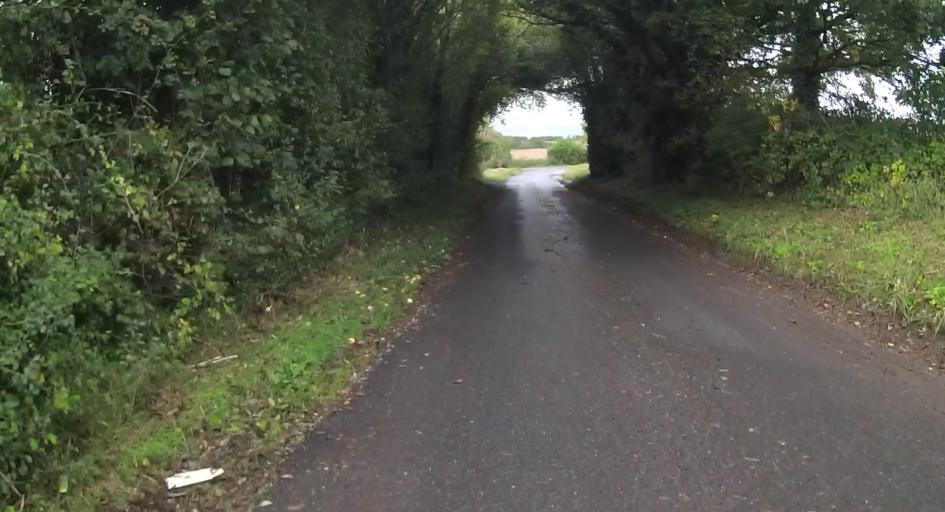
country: GB
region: England
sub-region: Hampshire
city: Basingstoke
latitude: 51.2767
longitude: -1.1465
